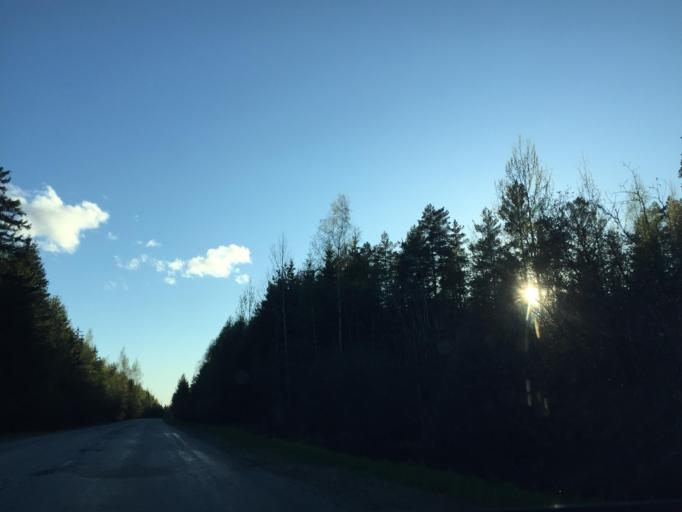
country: LV
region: Ergli
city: Ergli
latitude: 56.8702
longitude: 25.7978
